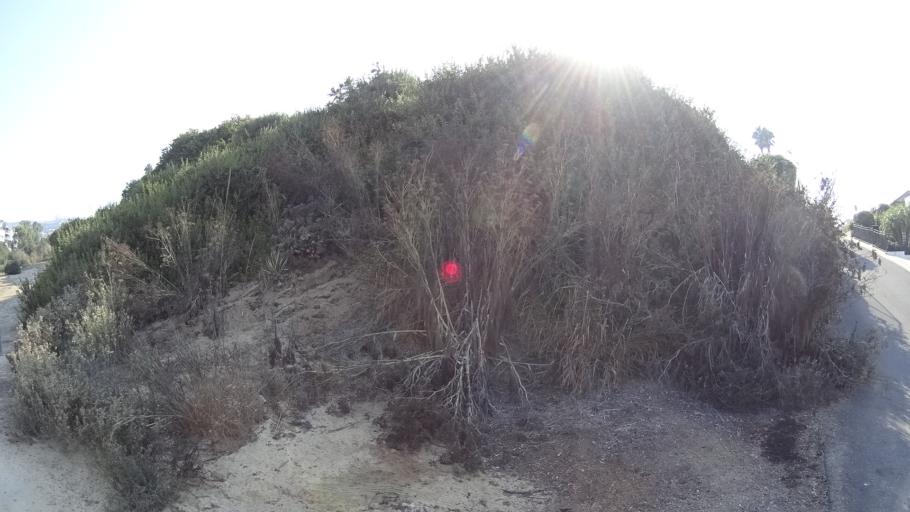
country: US
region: California
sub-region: Orange County
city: San Clemente
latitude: 33.4180
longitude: -117.6170
